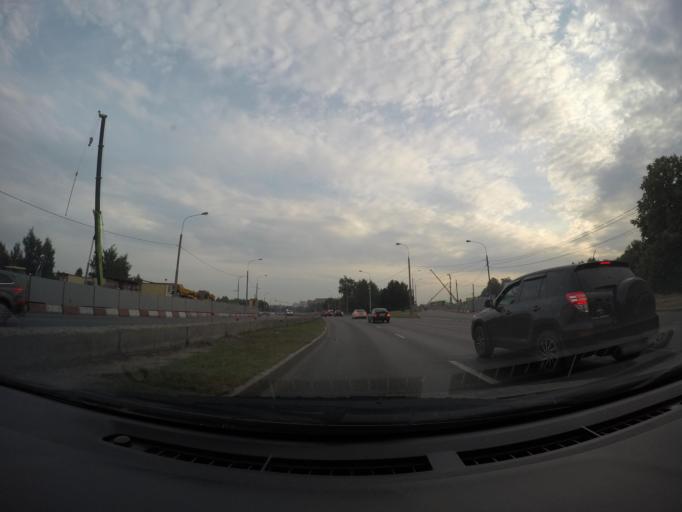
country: RU
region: Moscow
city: Kolomenskoye
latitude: 55.6595
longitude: 37.6541
